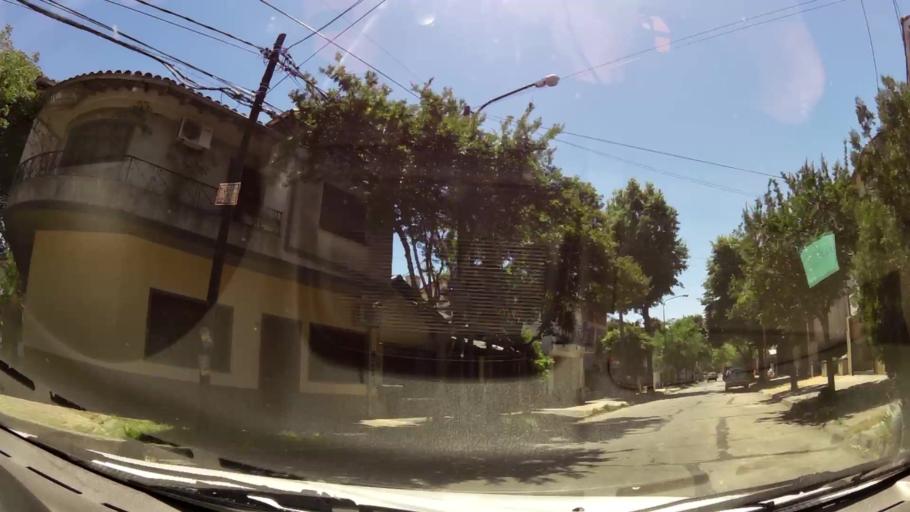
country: AR
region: Buenos Aires
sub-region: Partido de Vicente Lopez
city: Olivos
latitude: -34.5029
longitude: -58.5001
